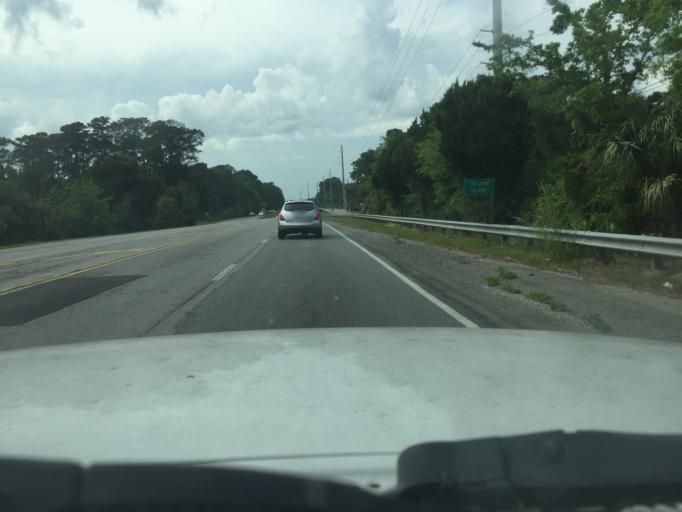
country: US
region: Georgia
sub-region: Chatham County
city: Whitemarsh Island
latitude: 32.0514
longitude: -81.0127
